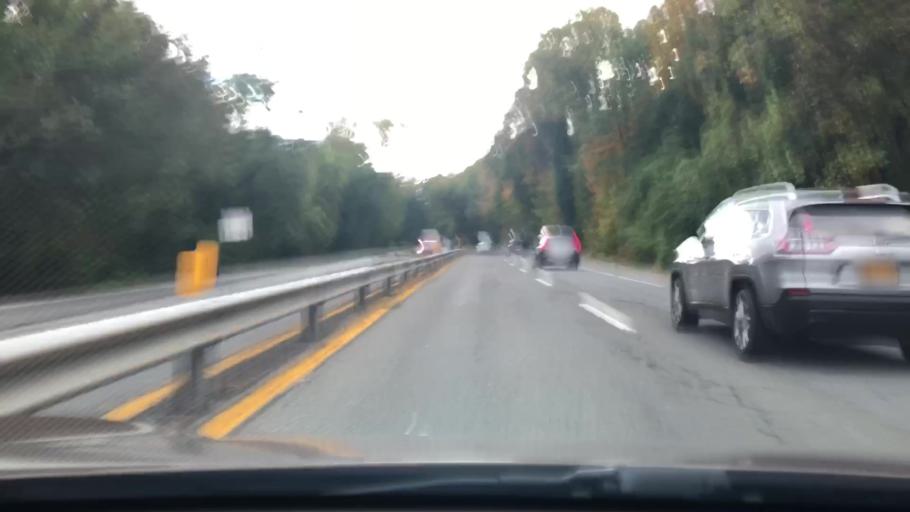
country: US
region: New York
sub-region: Westchester County
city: Tuckahoe
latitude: 40.9513
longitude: -73.8331
